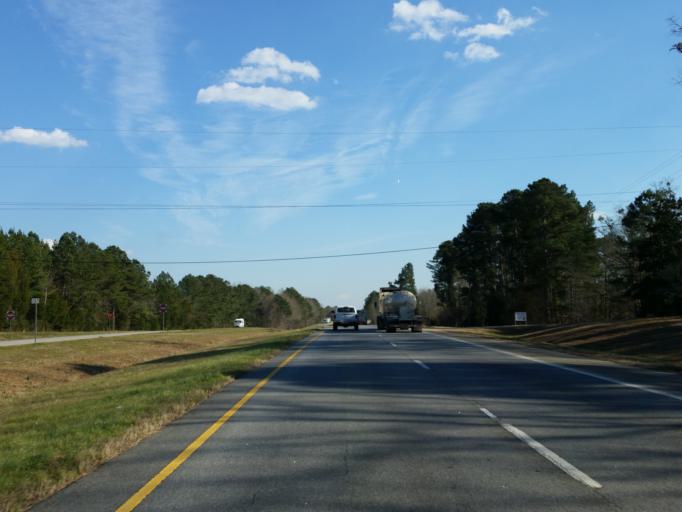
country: US
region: Georgia
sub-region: Spalding County
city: East Griffin
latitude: 33.1463
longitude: -84.2455
